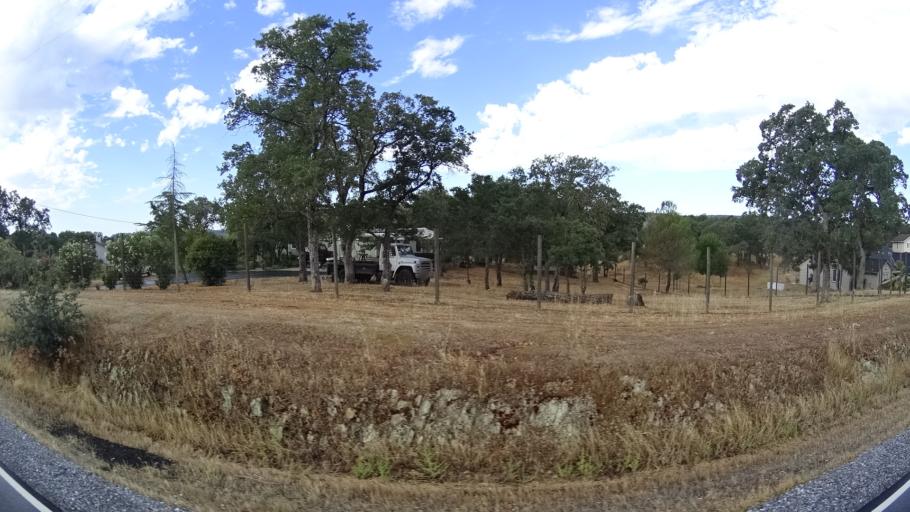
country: US
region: California
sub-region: Calaveras County
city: Copperopolis
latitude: 37.9188
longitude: -120.6287
